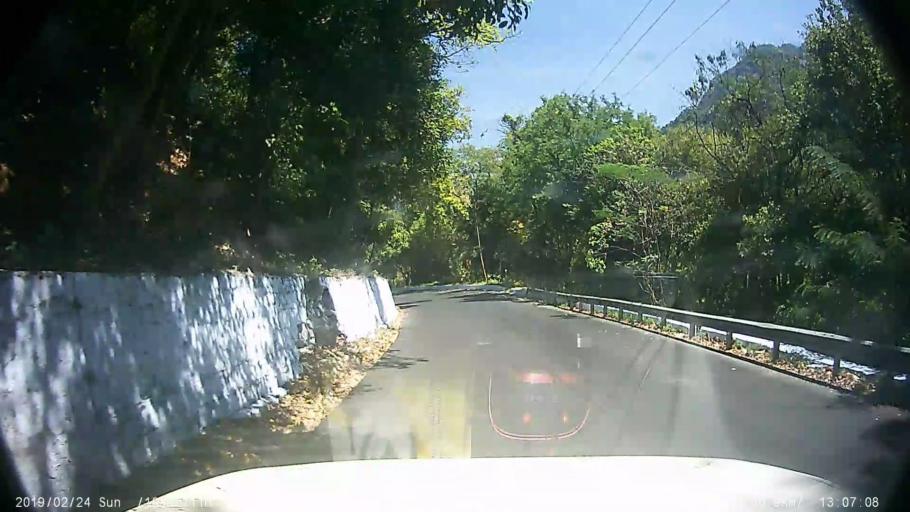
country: IN
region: Tamil Nadu
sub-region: Nilgiri
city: Wellington
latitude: 11.3377
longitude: 76.8324
